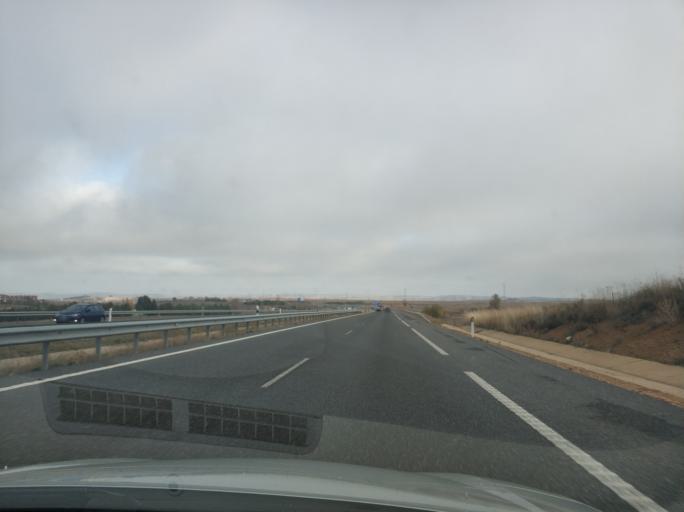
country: ES
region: Castille and Leon
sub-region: Provincia de Leon
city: Valdefresno
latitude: 42.5625
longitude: -5.5066
